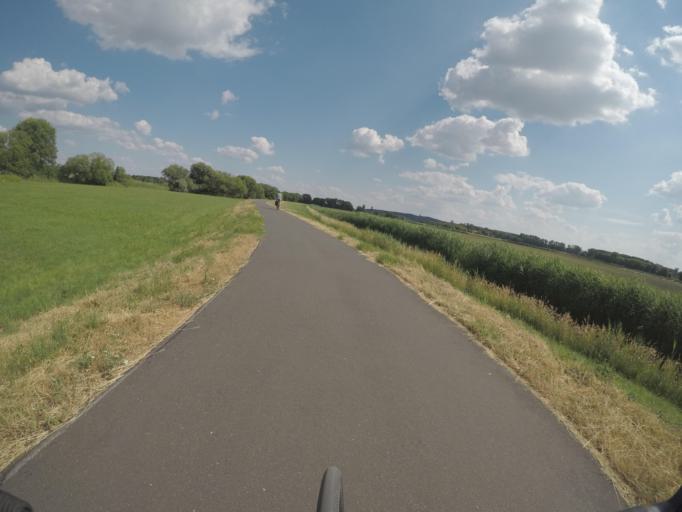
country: DE
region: Brandenburg
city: Ketzin
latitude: 52.4474
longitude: 12.8726
